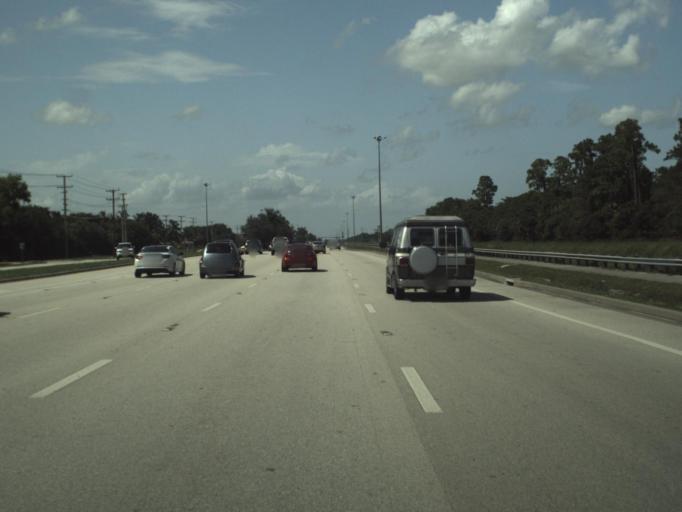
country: US
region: Florida
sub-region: Palm Beach County
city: Wellington
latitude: 26.6193
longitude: -80.2047
